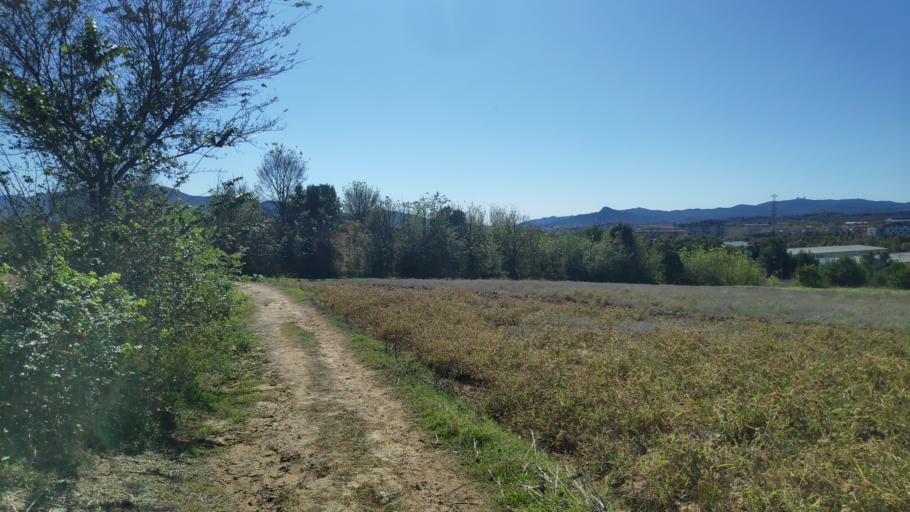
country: ES
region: Catalonia
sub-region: Provincia de Barcelona
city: Santa Perpetua de Mogoda
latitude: 41.5400
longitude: 2.1919
